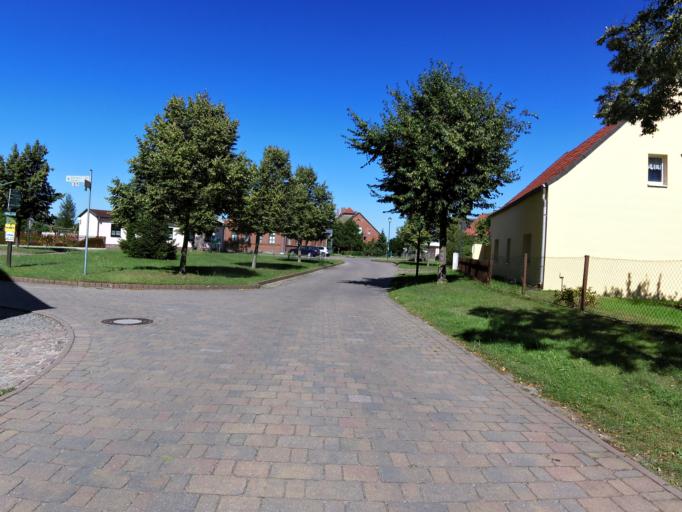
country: DE
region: Saxony-Anhalt
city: Muhlanger
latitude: 51.8373
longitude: 12.7579
